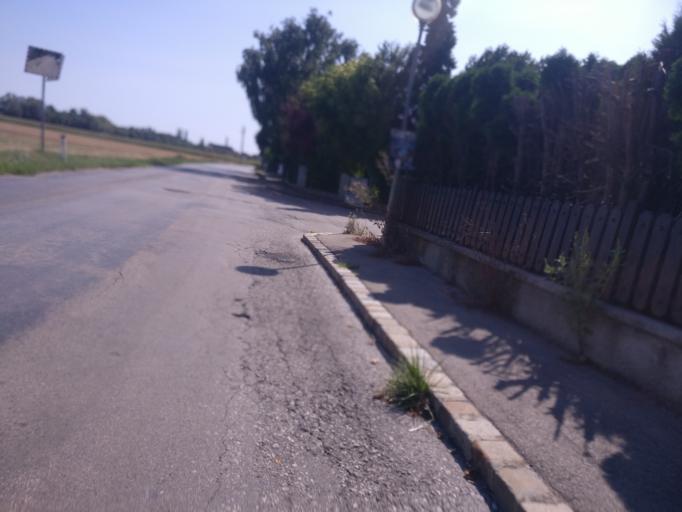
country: AT
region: Lower Austria
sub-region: Politischer Bezirk Modling
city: Guntramsdorf
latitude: 48.0378
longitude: 16.3105
